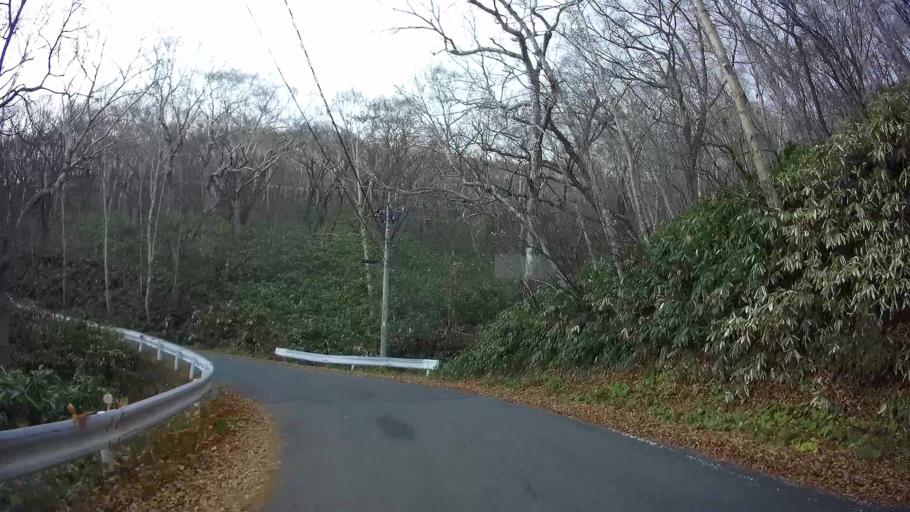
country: JP
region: Gunma
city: Nakanojomachi
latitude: 36.6888
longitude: 138.6525
